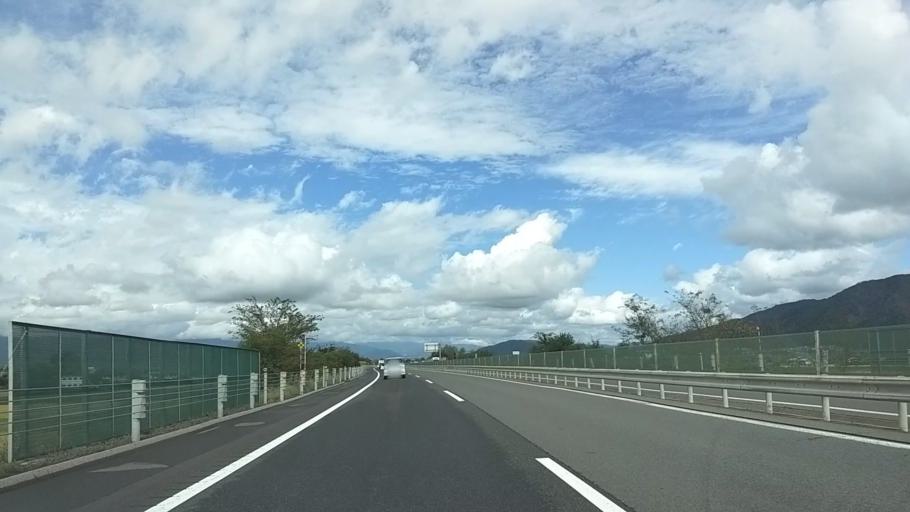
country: JP
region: Nagano
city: Toyoshina
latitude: 36.2833
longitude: 137.9305
